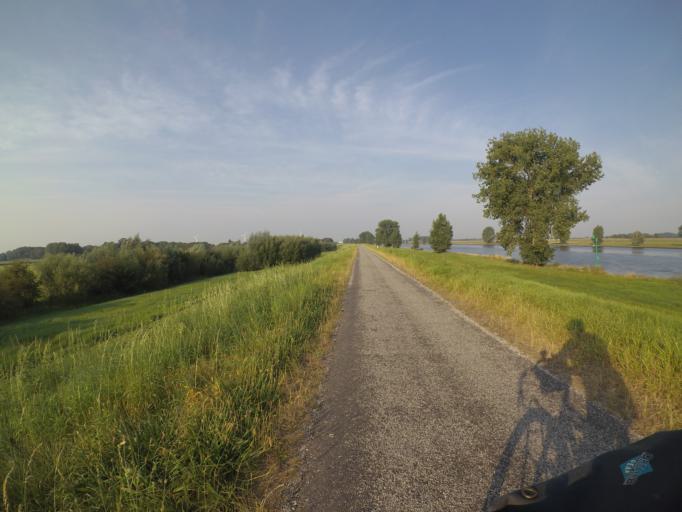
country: NL
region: North Brabant
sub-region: Gemeente Heusden
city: Heusden
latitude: 51.7266
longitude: 5.0934
